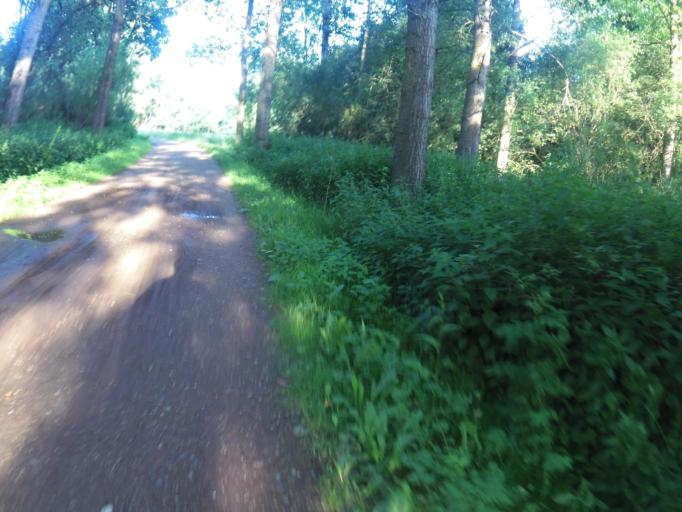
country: BE
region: Flanders
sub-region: Provincie Antwerpen
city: Herselt
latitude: 50.9993
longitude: 4.9009
